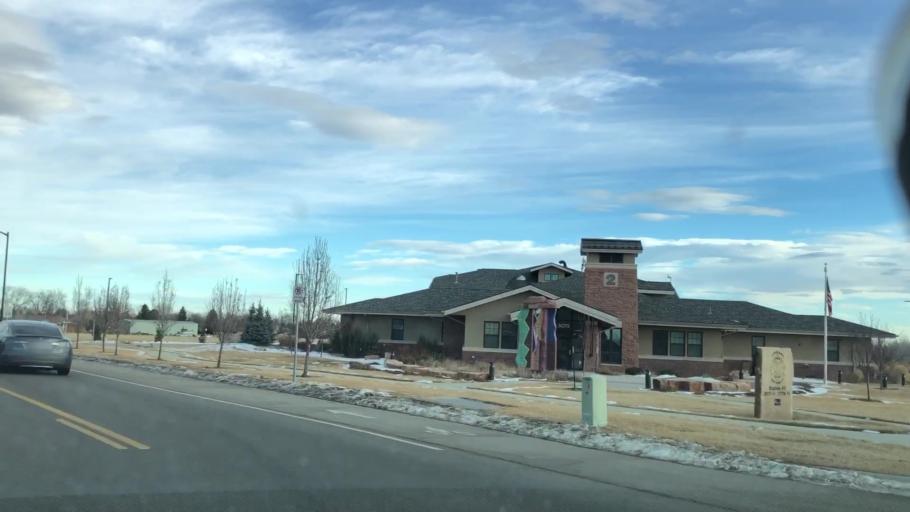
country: US
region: Colorado
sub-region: Larimer County
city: Loveland
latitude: 40.4218
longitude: -105.1204
